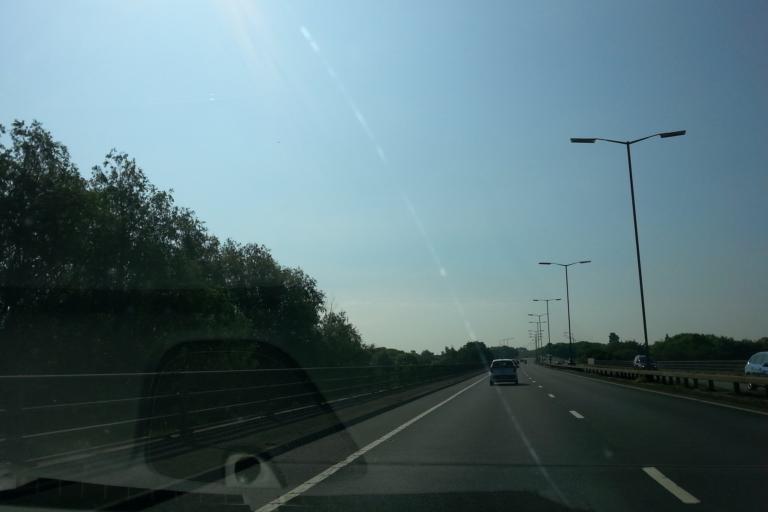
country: GB
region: England
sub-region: Peterborough
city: Peterborough
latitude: 52.5615
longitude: -0.2813
